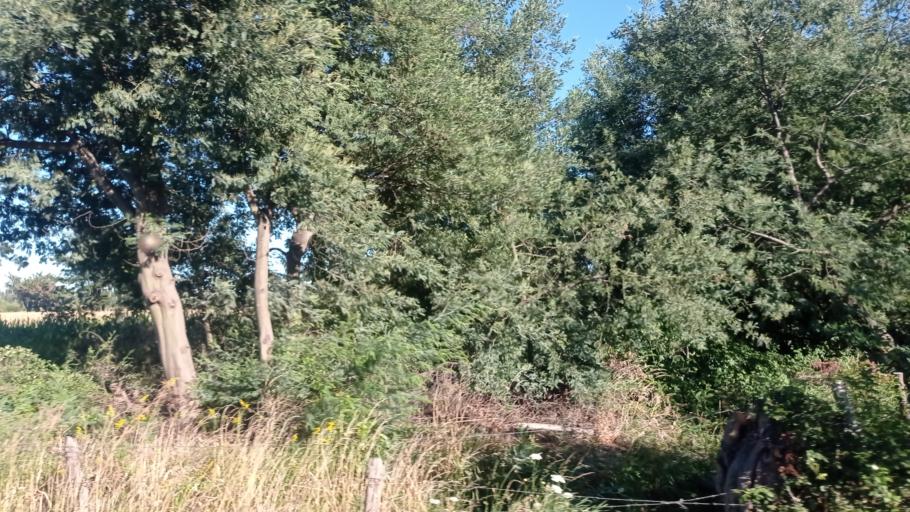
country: CL
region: Biobio
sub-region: Provincia de Biobio
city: Los Angeles
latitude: -37.5111
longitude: -72.4990
